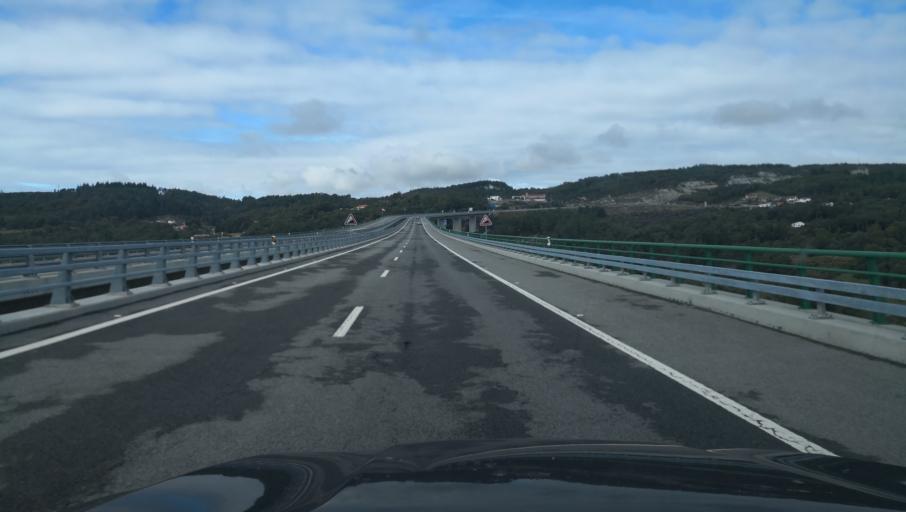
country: PT
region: Vila Real
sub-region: Vila Pouca de Aguiar
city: Vila Pouca de Aguiar
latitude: 41.4811
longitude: -7.6519
